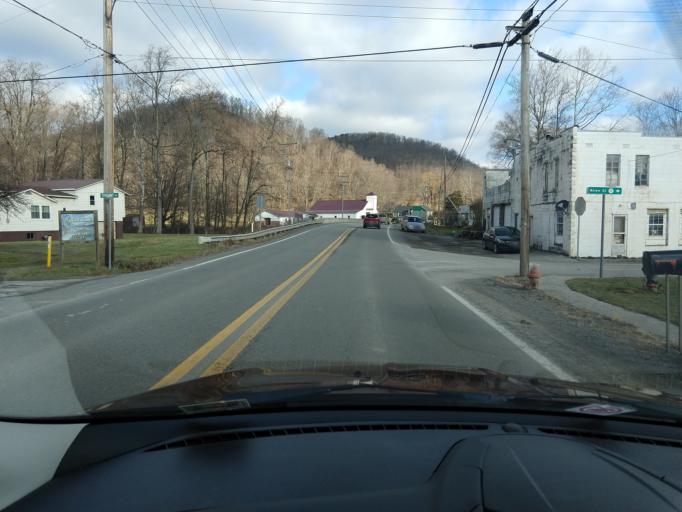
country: US
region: West Virginia
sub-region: Randolph County
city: Elkins
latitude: 38.7334
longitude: -79.9696
